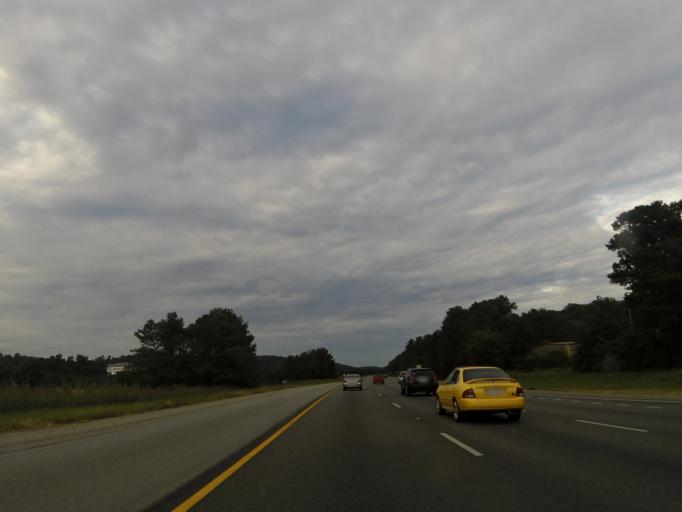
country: US
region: Alabama
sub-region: Shelby County
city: Pelham
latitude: 33.2890
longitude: -86.7997
